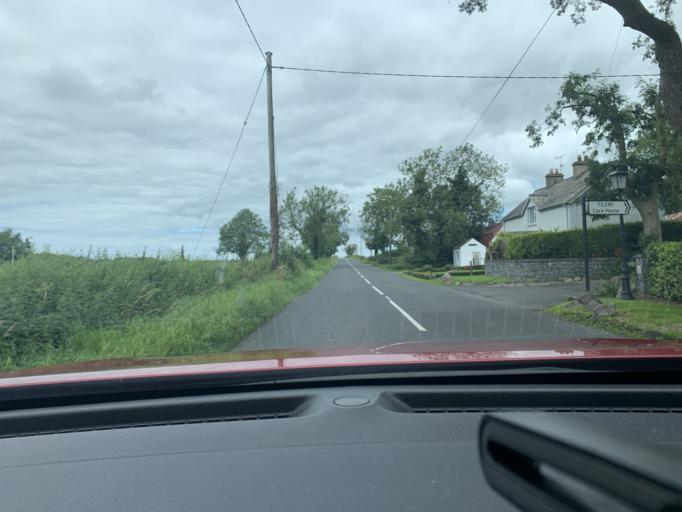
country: GB
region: Northern Ireland
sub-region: Fermanagh District
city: Enniskillen
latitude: 54.2810
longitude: -7.7016
